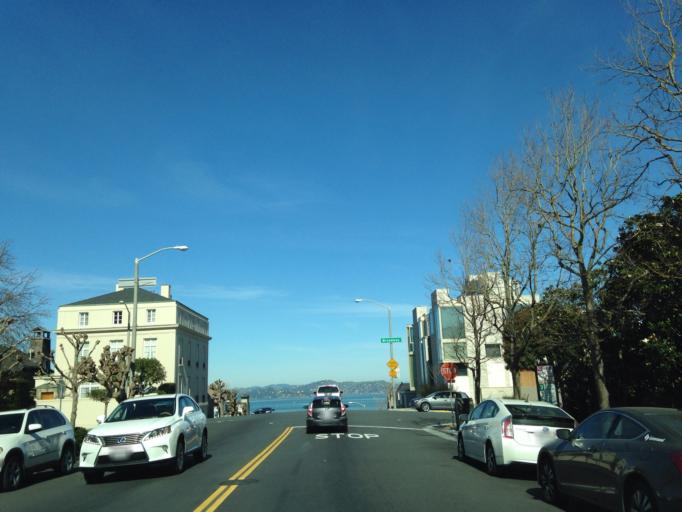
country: US
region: California
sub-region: San Francisco County
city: San Francisco
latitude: 37.7930
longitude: -122.4414
